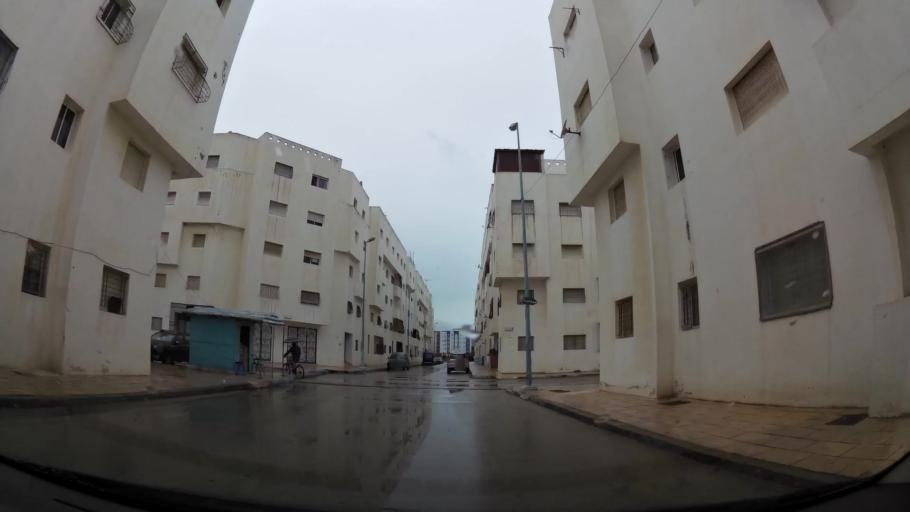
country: MA
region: Tanger-Tetouan
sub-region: Tetouan
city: Martil
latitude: 35.6182
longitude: -5.2848
